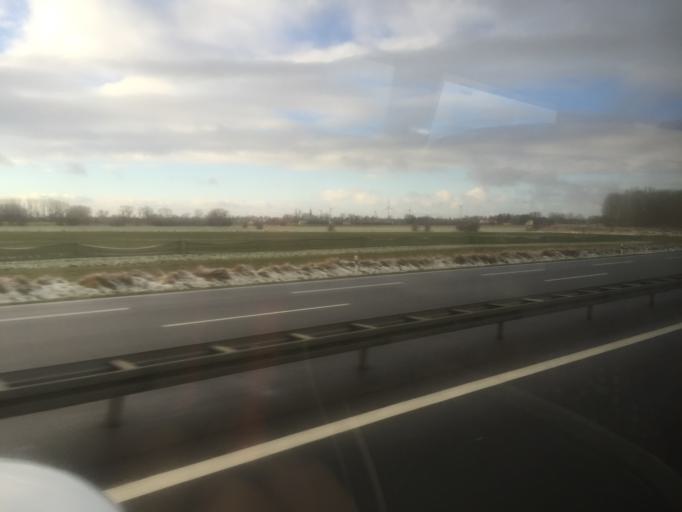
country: DE
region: Brandenburg
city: Dabergotz
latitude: 52.9019
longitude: 12.7434
